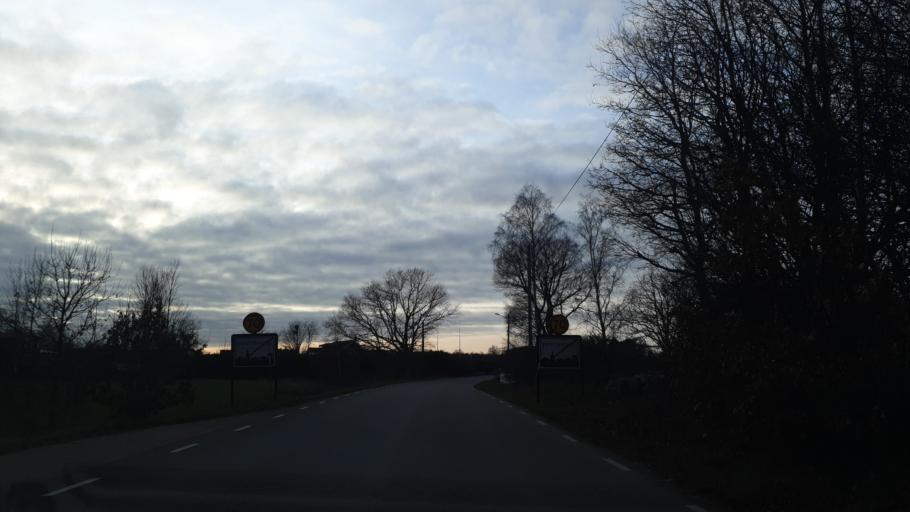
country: SE
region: Kalmar
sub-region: Torsas Kommun
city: Torsas
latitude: 56.2563
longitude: 16.0353
